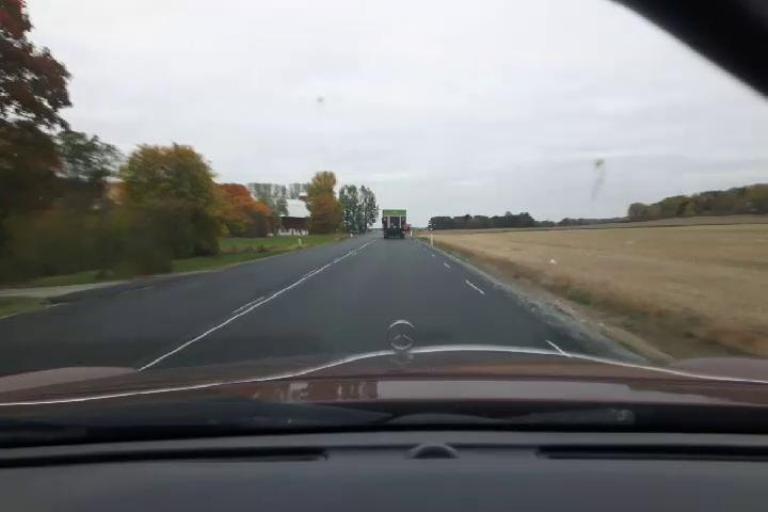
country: SE
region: Uppsala
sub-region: Enkopings Kommun
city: Enkoping
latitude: 59.6053
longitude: 17.0228
